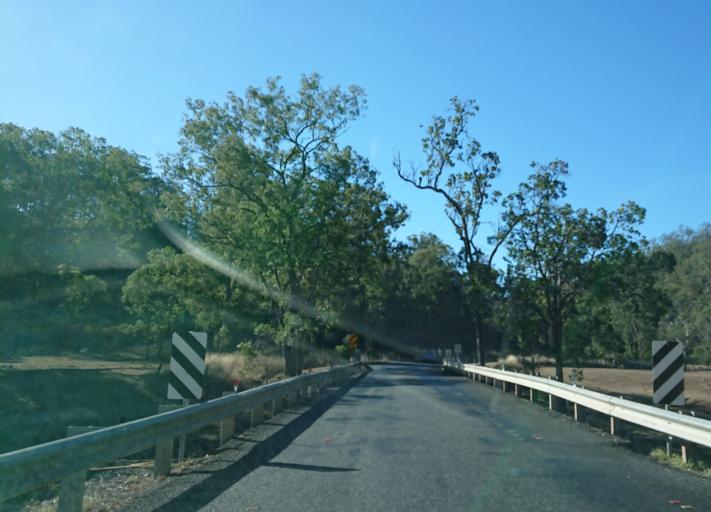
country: AU
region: Queensland
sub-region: Toowoomba
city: Top Camp
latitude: -27.7589
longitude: 152.0818
